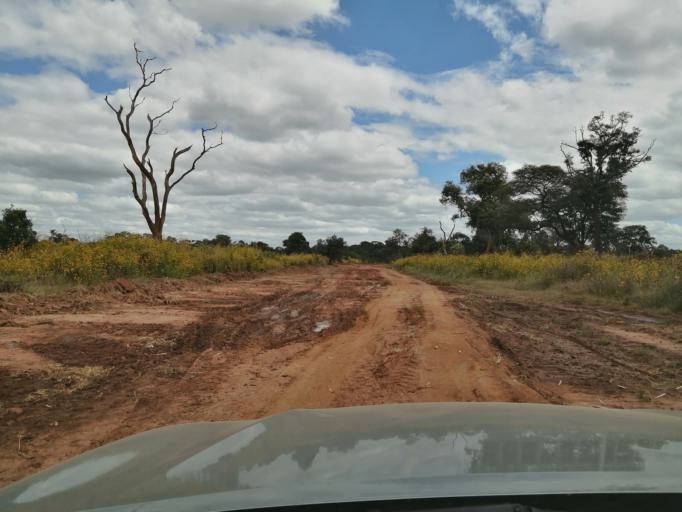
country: ZM
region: Central
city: Mumbwa
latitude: -14.5829
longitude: 27.2168
